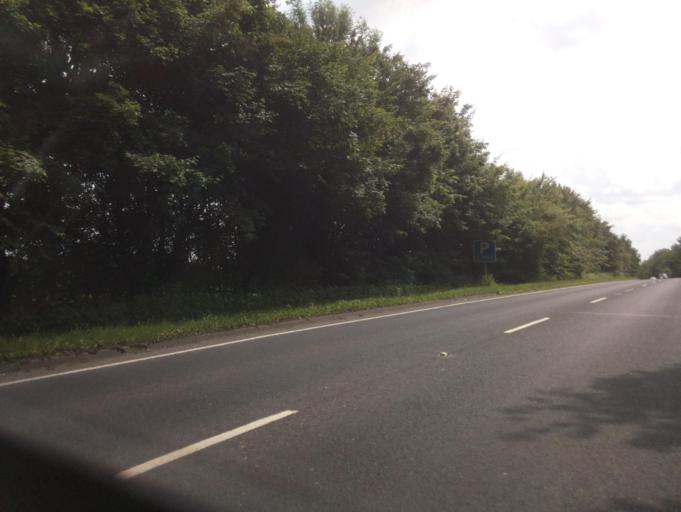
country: GB
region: England
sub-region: North Yorkshire
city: Boroughbridge
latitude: 54.0910
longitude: -1.4039
